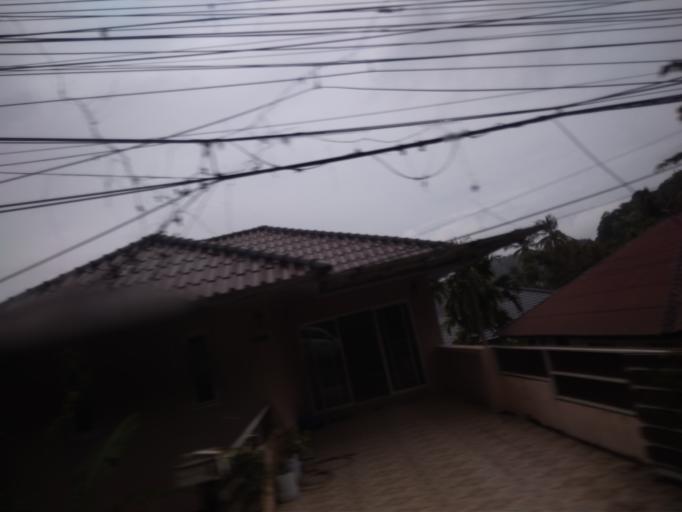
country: TH
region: Phuket
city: Mueang Phuket
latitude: 7.8149
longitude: 98.3964
